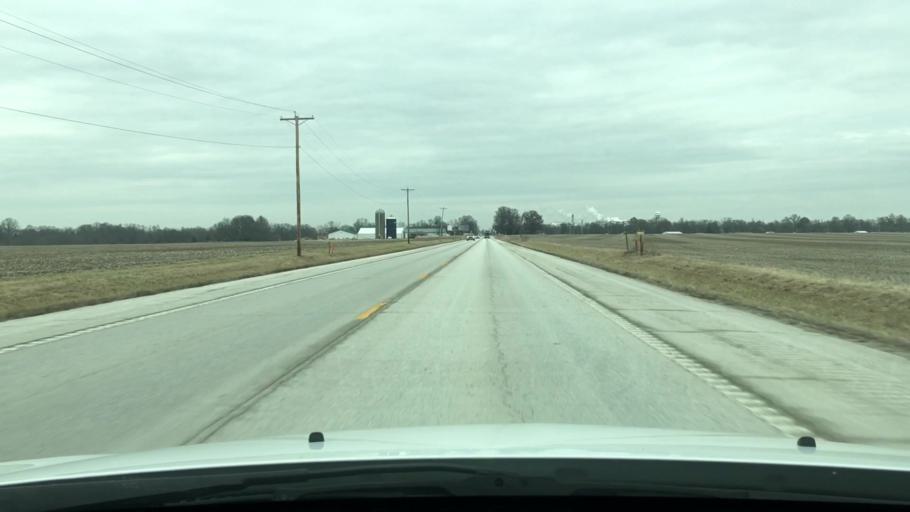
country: US
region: Missouri
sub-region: Montgomery County
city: Wellsville
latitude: 39.2291
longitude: -91.6460
